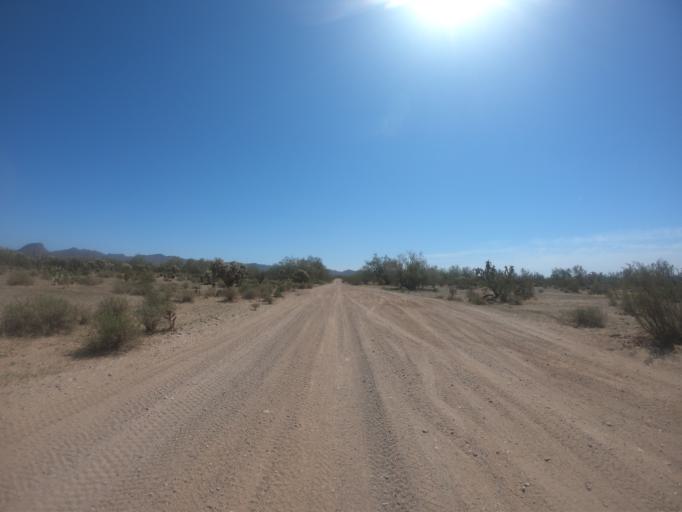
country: US
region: Arizona
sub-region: Pinal County
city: Gold Camp
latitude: 33.2346
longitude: -111.3027
